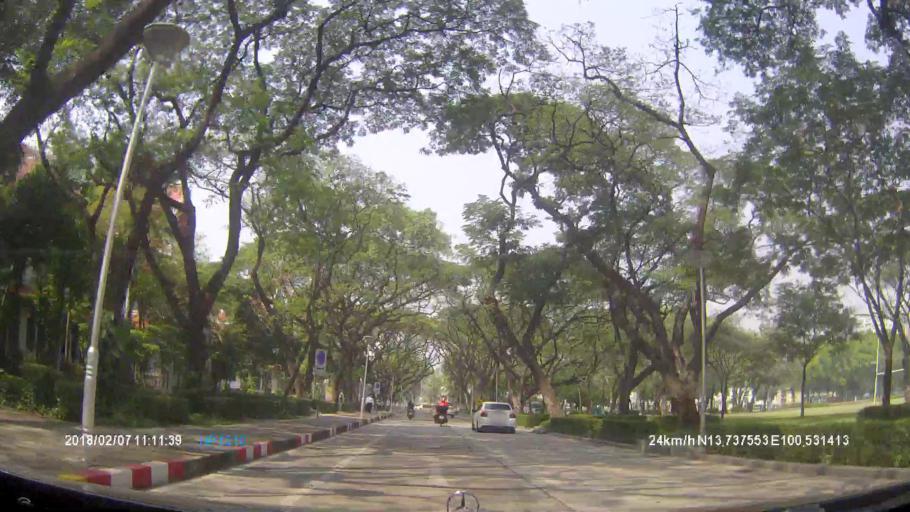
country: TH
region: Bangkok
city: Pathum Wan
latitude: 13.7376
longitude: 100.5313
